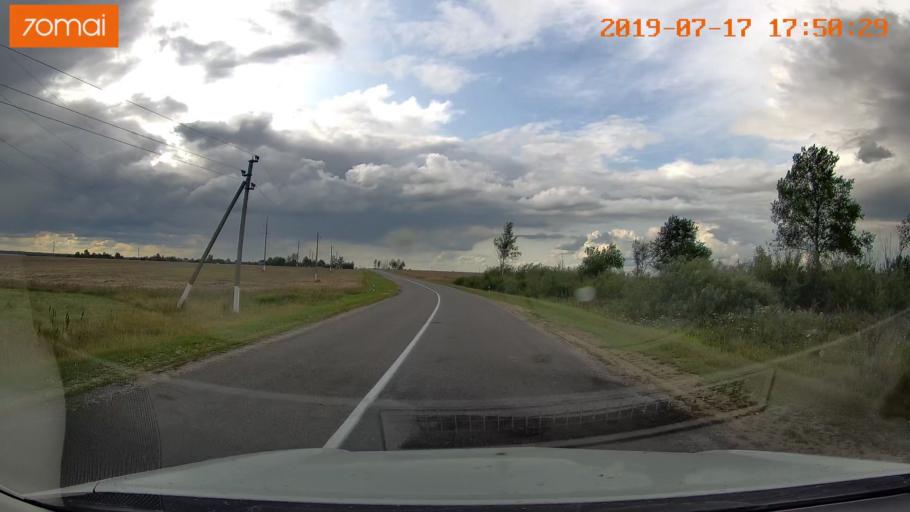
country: BY
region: Mogilev
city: Hlusha
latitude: 53.1419
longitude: 28.8016
